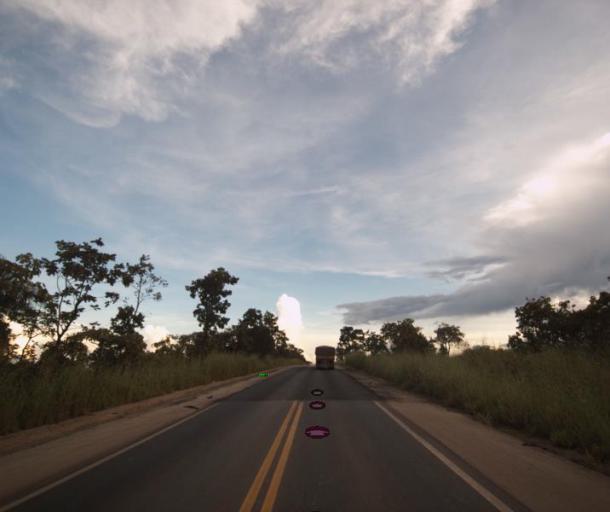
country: BR
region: Goias
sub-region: Uruacu
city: Uruacu
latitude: -14.2320
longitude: -49.1343
